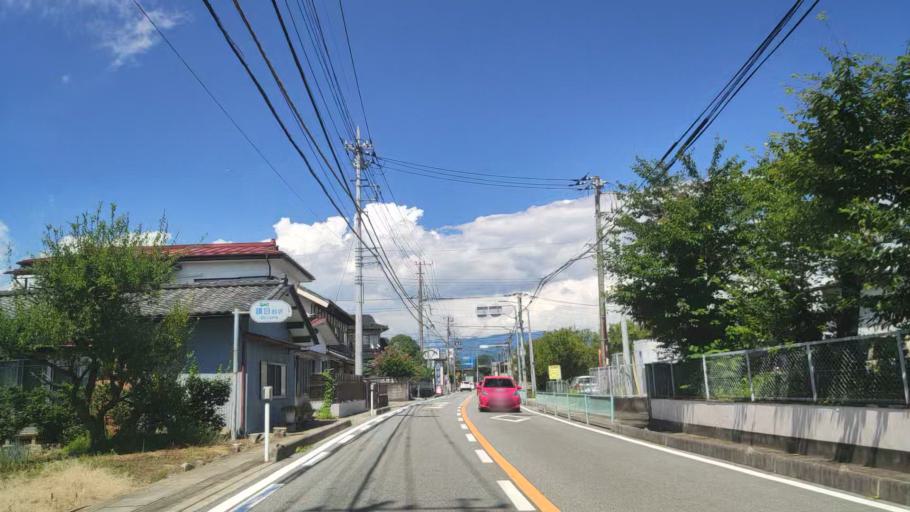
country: JP
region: Yamanashi
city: Isawa
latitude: 35.6643
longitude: 138.6432
